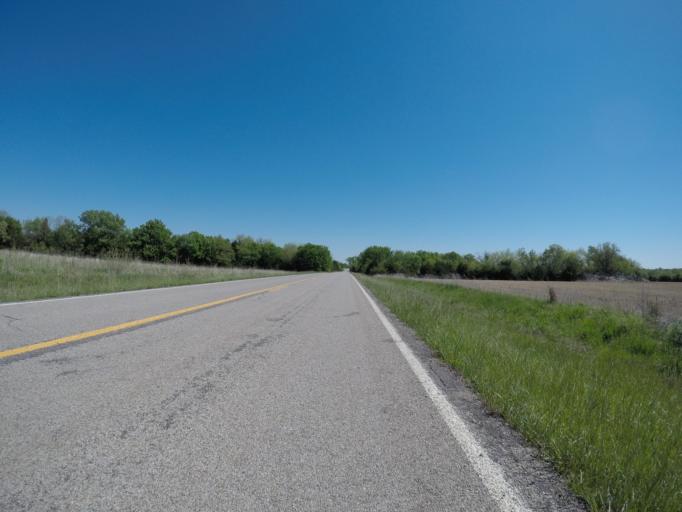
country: US
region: Kansas
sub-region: Osage County
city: Overbrook
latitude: 38.8794
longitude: -95.5440
